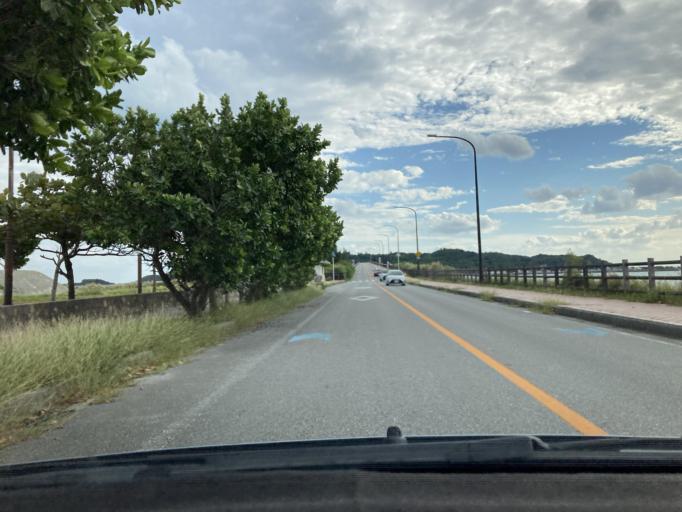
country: JP
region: Okinawa
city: Katsuren-haebaru
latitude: 26.3384
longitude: 127.9549
